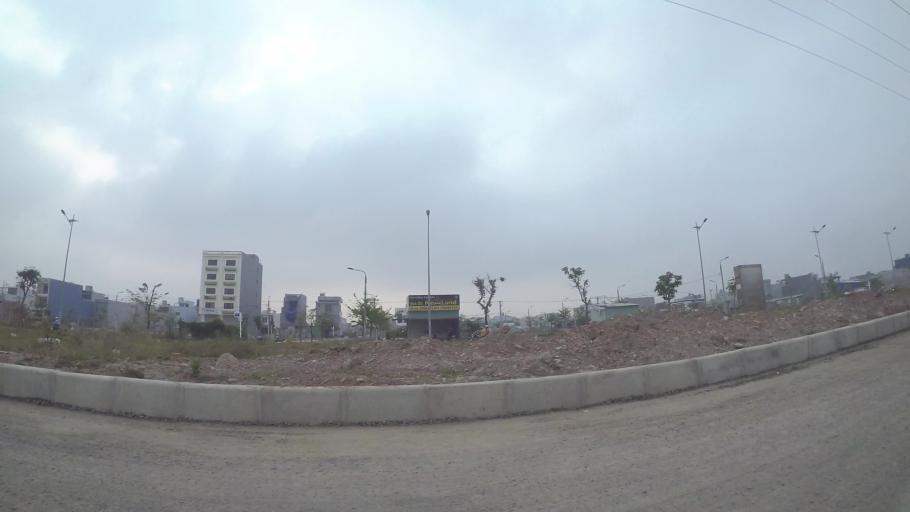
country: VN
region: Da Nang
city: Cam Le
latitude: 16.0128
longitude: 108.2251
